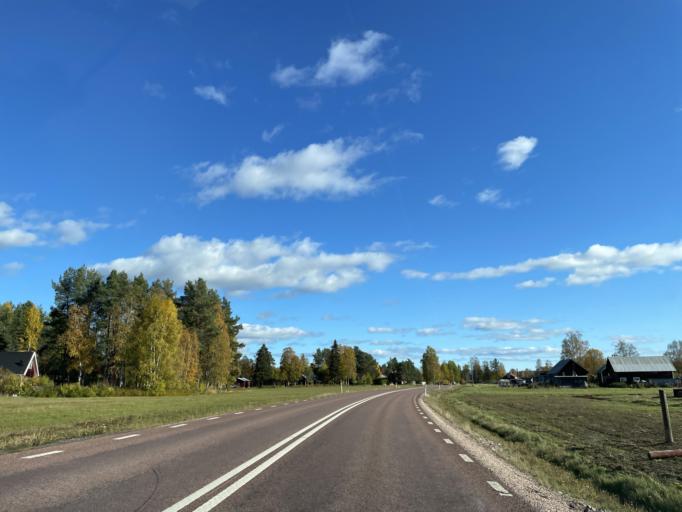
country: SE
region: Dalarna
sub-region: Malung-Saelens kommun
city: Malung
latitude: 60.7040
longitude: 13.6808
